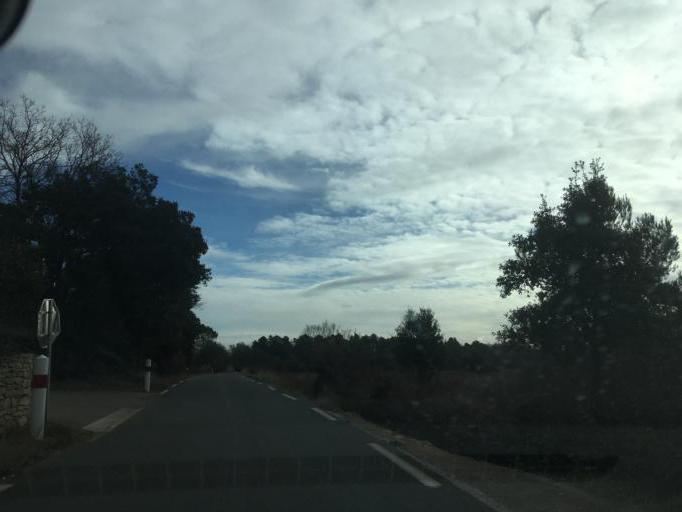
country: FR
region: Provence-Alpes-Cote d'Azur
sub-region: Departement du Var
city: Bras
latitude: 43.4529
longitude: 5.9748
